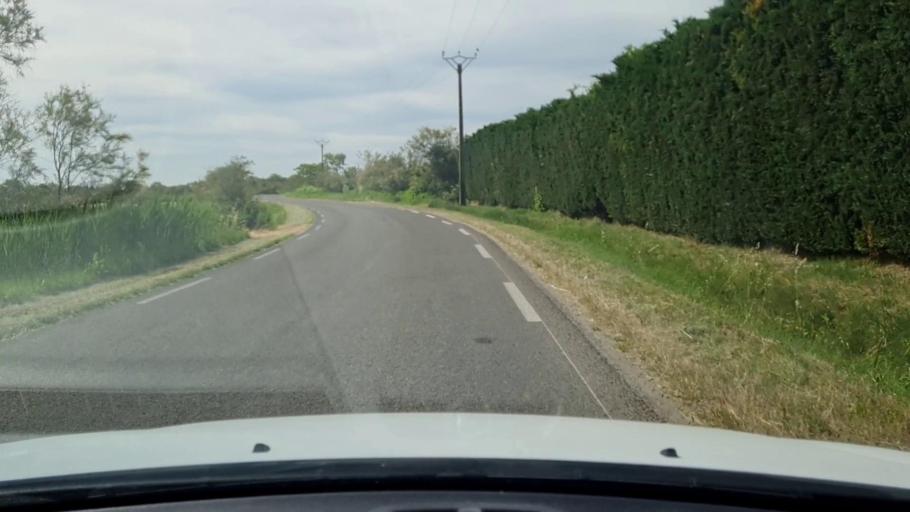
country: FR
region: Languedoc-Roussillon
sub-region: Departement du Gard
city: Aigues-Mortes
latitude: 43.6110
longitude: 4.2104
